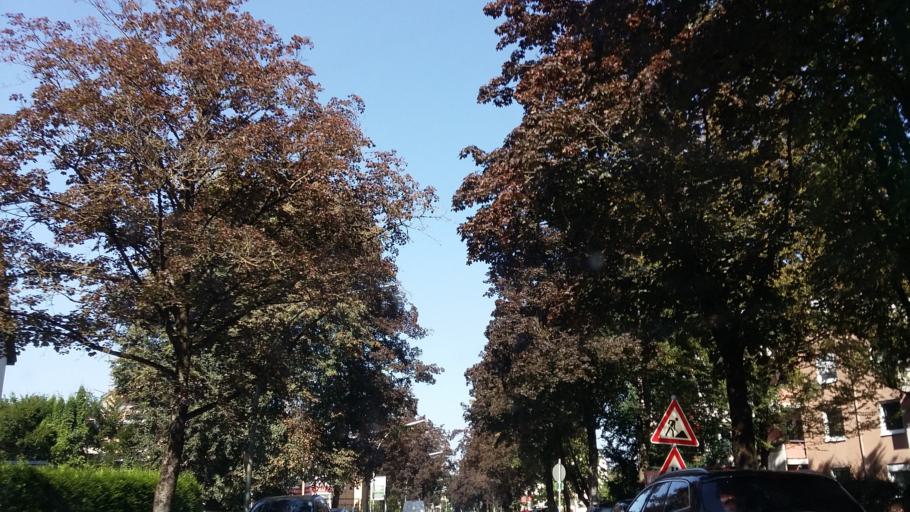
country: DE
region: Bavaria
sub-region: Swabia
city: Augsburg
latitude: 48.3405
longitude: 10.8771
